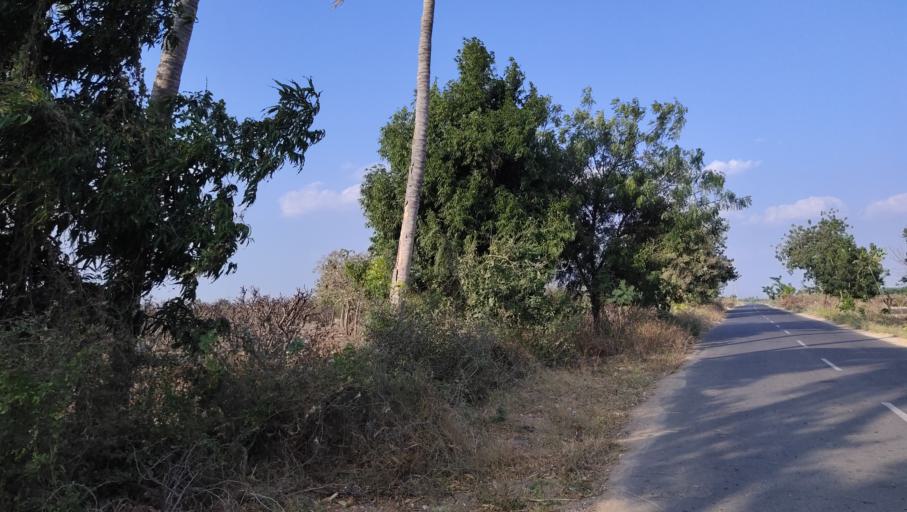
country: IN
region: Andhra Pradesh
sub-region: Anantapur
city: Tadpatri
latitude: 14.9459
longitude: 77.8763
